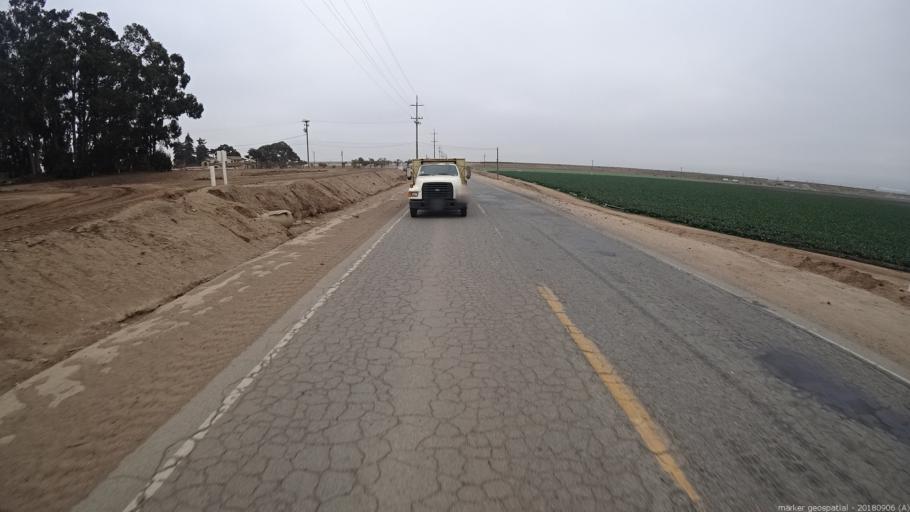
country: US
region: California
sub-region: Monterey County
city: Salinas
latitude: 36.6629
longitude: -121.5923
